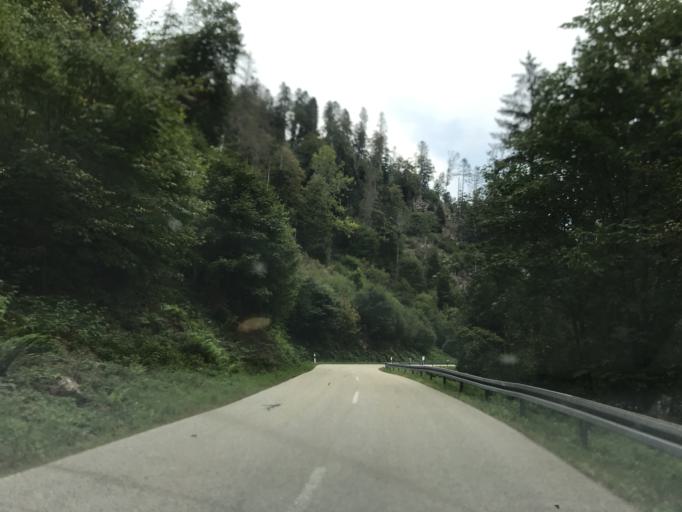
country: DE
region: Baden-Wuerttemberg
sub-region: Freiburg Region
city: Herrischried
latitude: 47.6824
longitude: 7.9508
